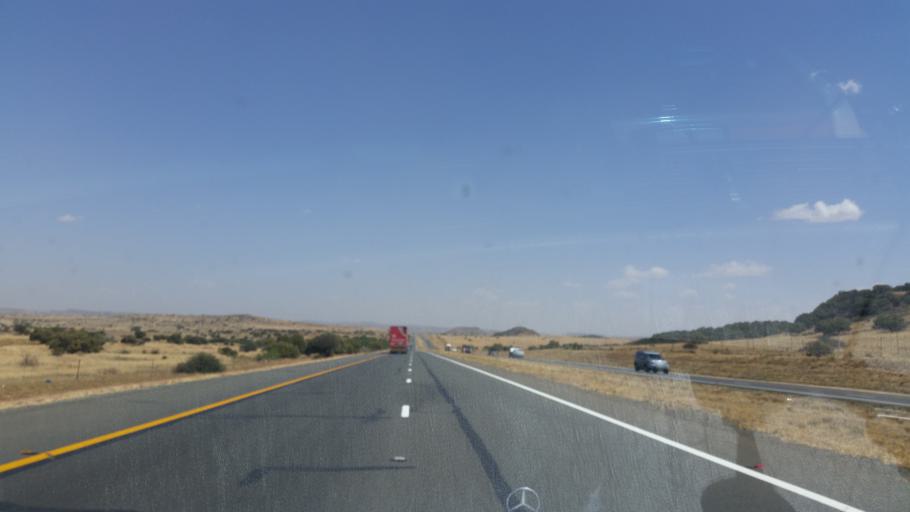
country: ZA
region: Orange Free State
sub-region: Lejweleputswa District Municipality
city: Brandfort
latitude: -28.9185
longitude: 26.4444
